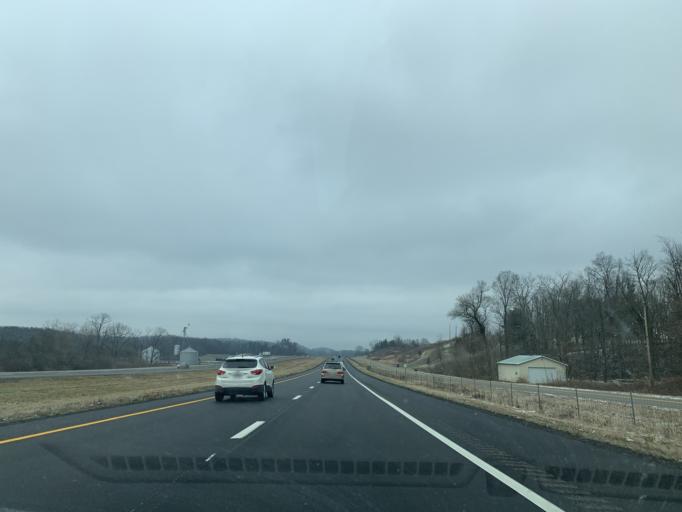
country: US
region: Ohio
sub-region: Licking County
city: Granville South
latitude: 40.0714
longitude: -82.5780
